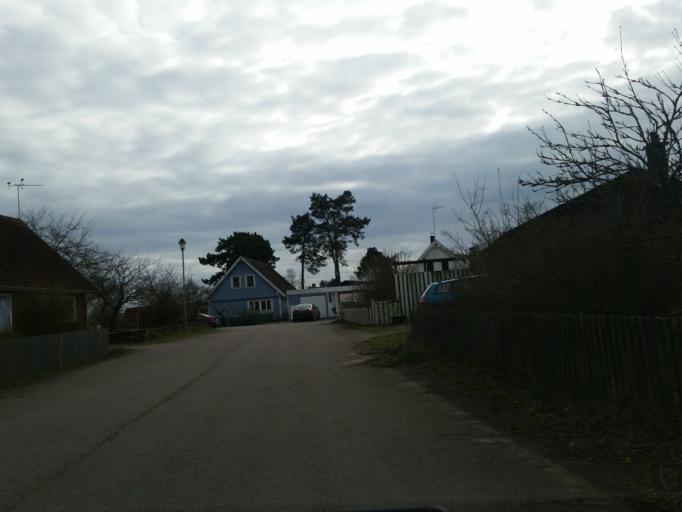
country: SE
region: Kalmar
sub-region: Morbylanga Kommun
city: Sodra Sandby
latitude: 56.6064
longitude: 16.6471
